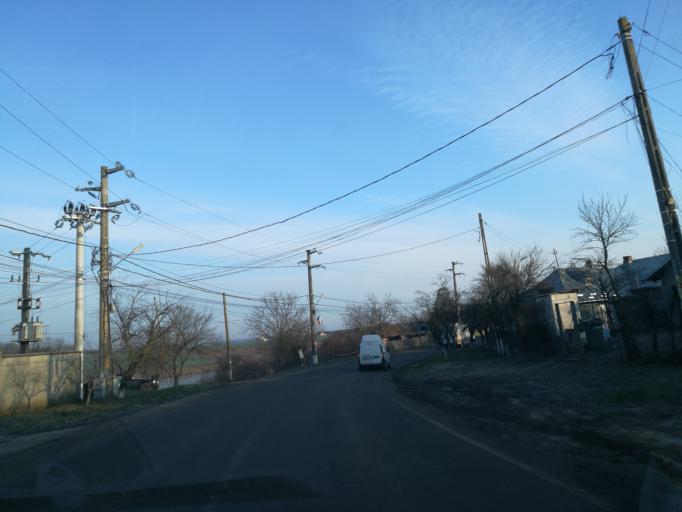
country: RO
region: Ilfov
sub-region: Comuna Moara Vlasiei
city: Caciulati
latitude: 44.6313
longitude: 26.1775
